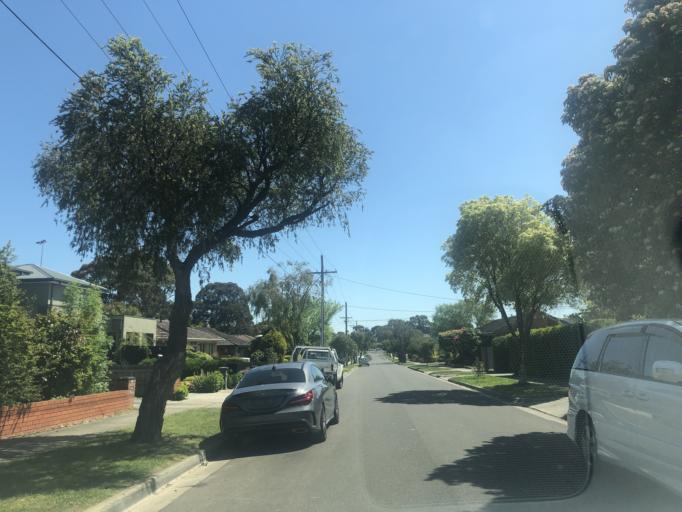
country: AU
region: Victoria
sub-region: Monash
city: Notting Hill
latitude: -37.9011
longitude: 145.1664
